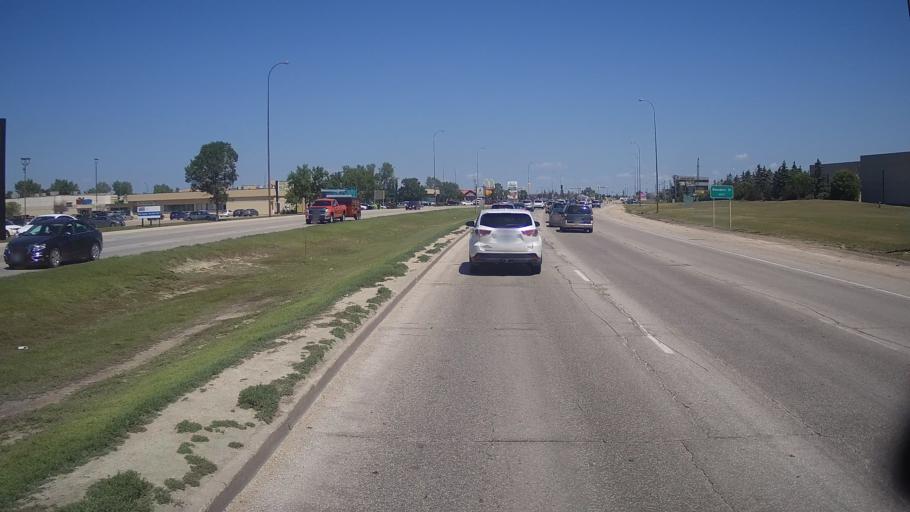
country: CA
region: Manitoba
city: Winnipeg
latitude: 49.9001
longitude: -97.0681
